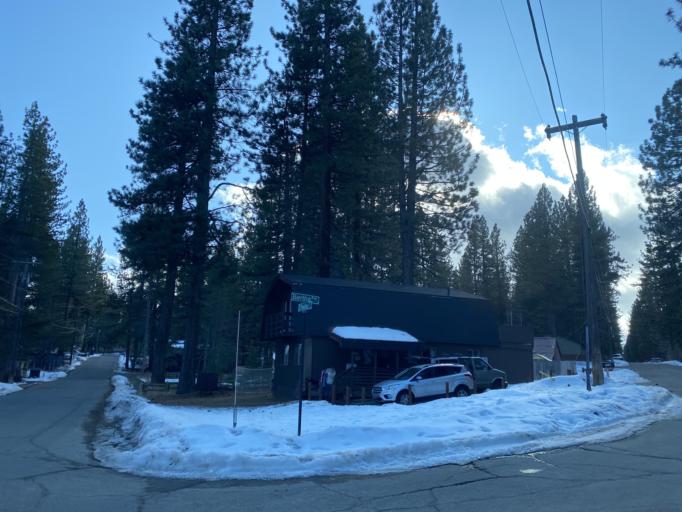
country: US
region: California
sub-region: El Dorado County
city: South Lake Tahoe
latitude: 38.9259
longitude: -119.9764
